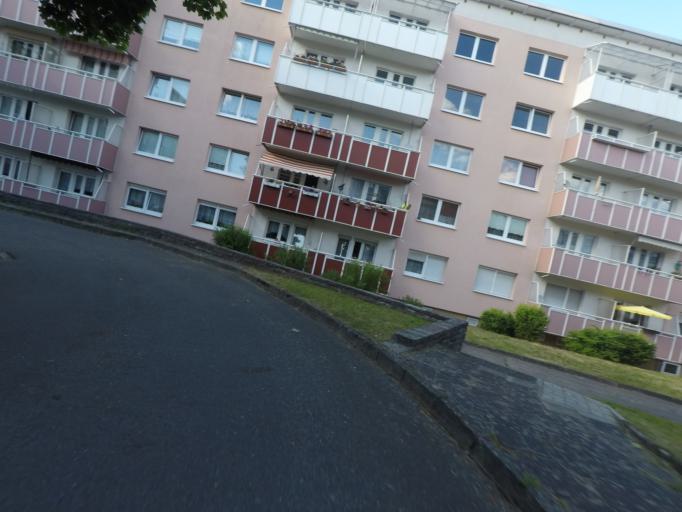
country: DE
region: Brandenburg
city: Eberswalde
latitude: 52.8405
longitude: 13.8114
